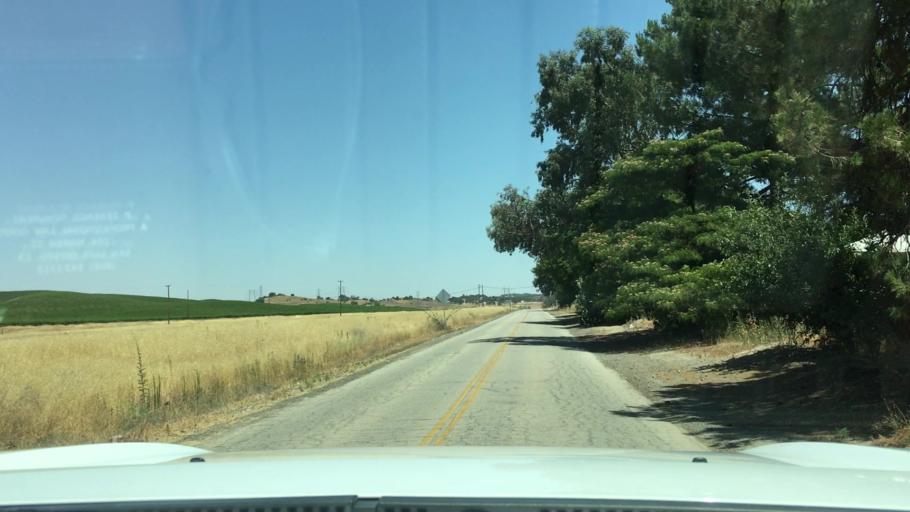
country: US
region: California
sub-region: San Luis Obispo County
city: Paso Robles
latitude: 35.6119
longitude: -120.6439
